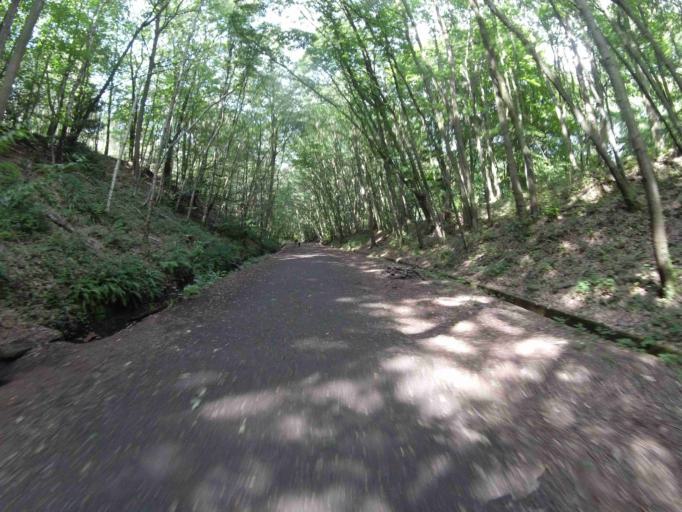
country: GB
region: England
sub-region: Devon
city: Budleigh Salterton
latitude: 50.6346
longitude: -3.3518
